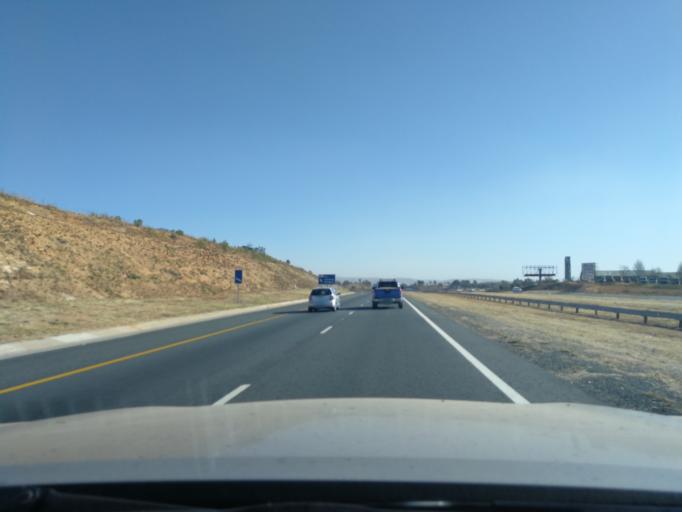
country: ZA
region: Gauteng
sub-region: West Rand District Municipality
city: Muldersdriseloop
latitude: -26.0163
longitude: 27.8704
